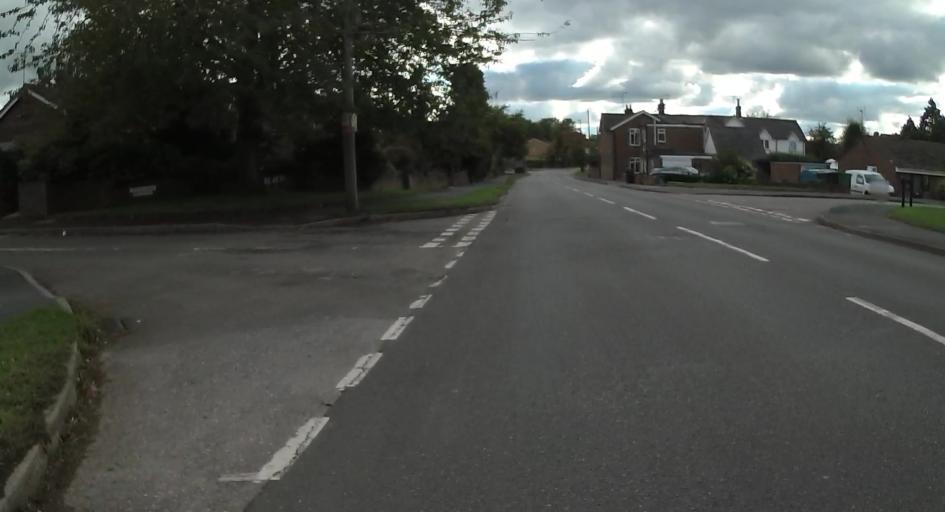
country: GB
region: England
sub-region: Surrey
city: Seale
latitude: 51.2370
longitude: -0.7310
